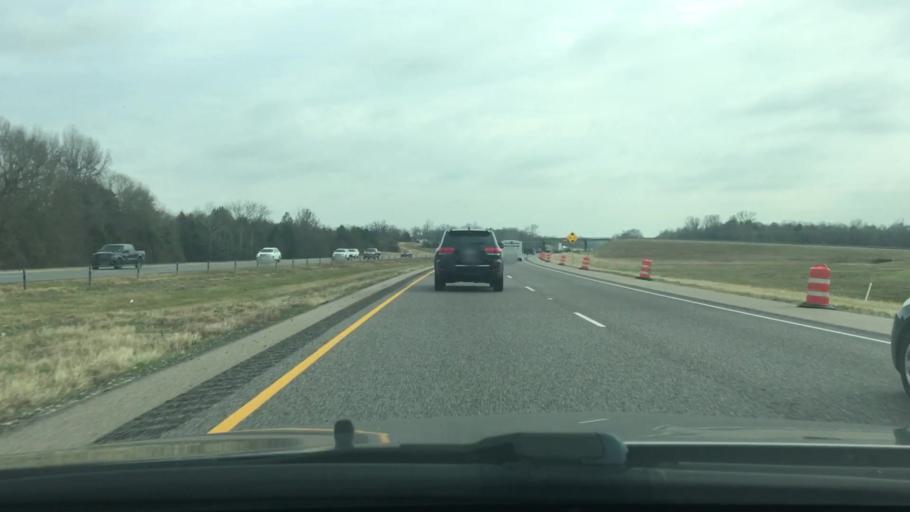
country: US
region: Texas
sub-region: Leon County
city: Buffalo
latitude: 31.5037
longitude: -96.0988
